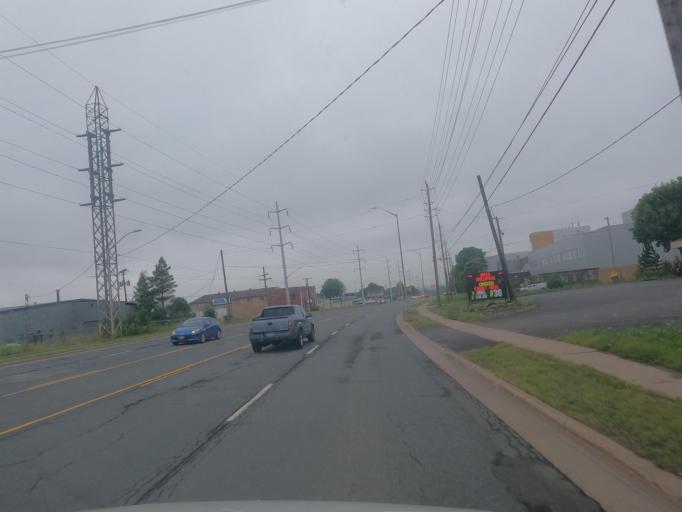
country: CA
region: Ontario
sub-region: Algoma
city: Sault Ste. Marie
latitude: 46.5382
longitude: -84.3320
